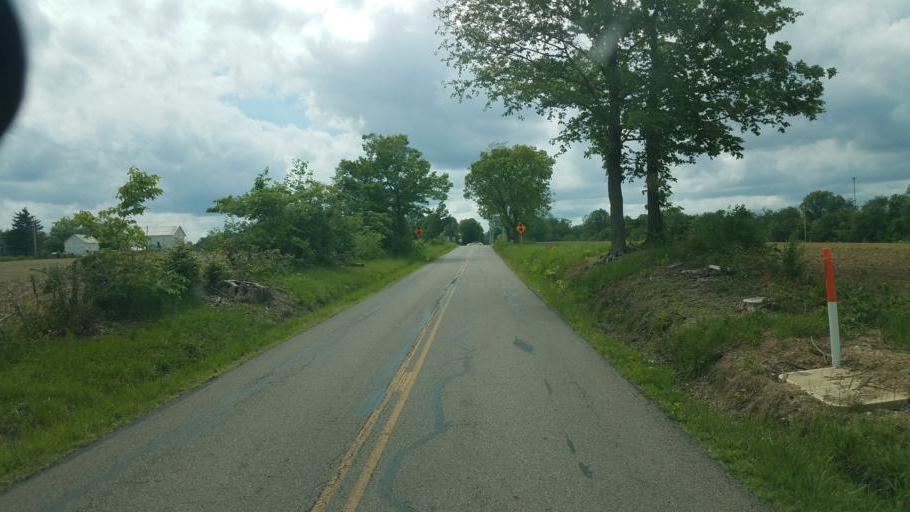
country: US
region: Ohio
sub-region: Fairfield County
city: Millersport
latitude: 39.9379
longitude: -82.5984
